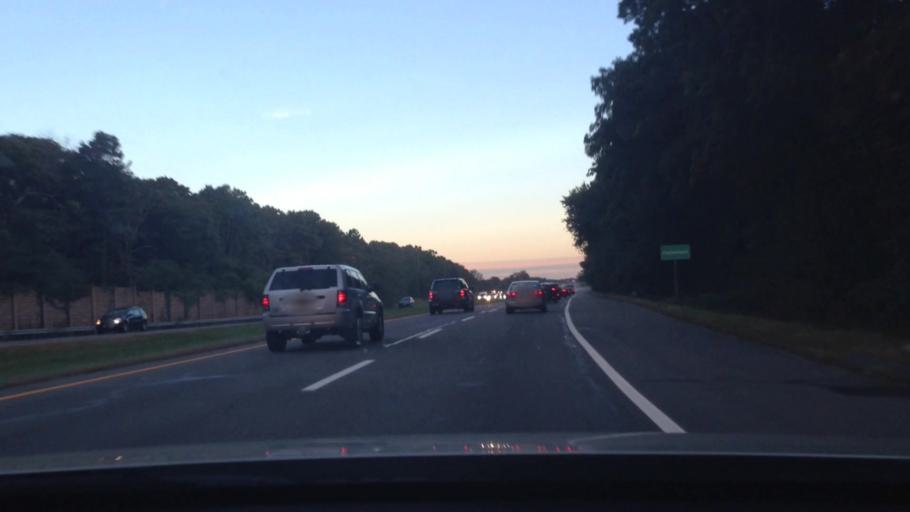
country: US
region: New York
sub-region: Suffolk County
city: Centereach
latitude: 40.8540
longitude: -73.0670
